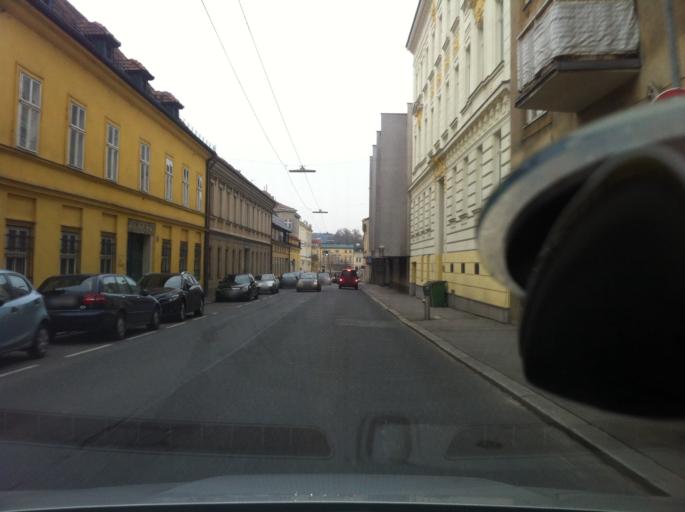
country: AT
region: Vienna
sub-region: Wien Stadt
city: Vienna
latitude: 48.1908
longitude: 16.3018
